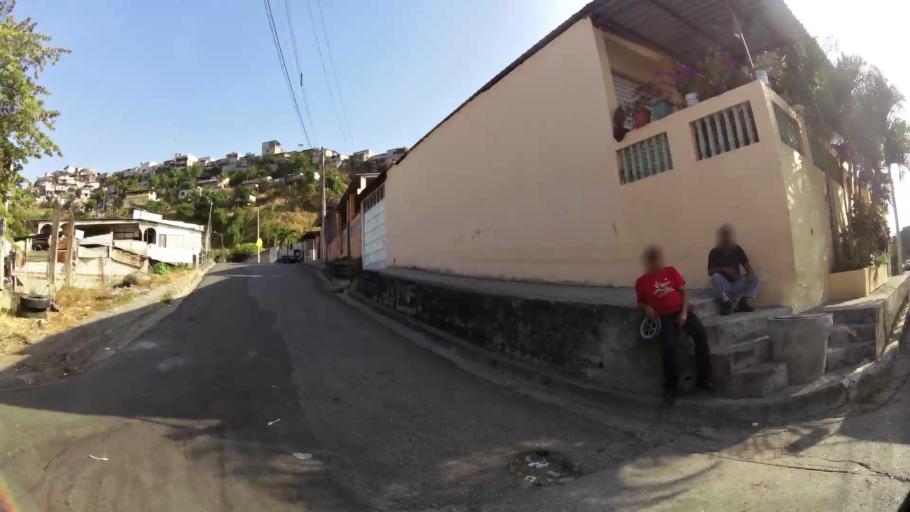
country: EC
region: Guayas
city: Guayaquil
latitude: -2.1430
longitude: -79.9301
